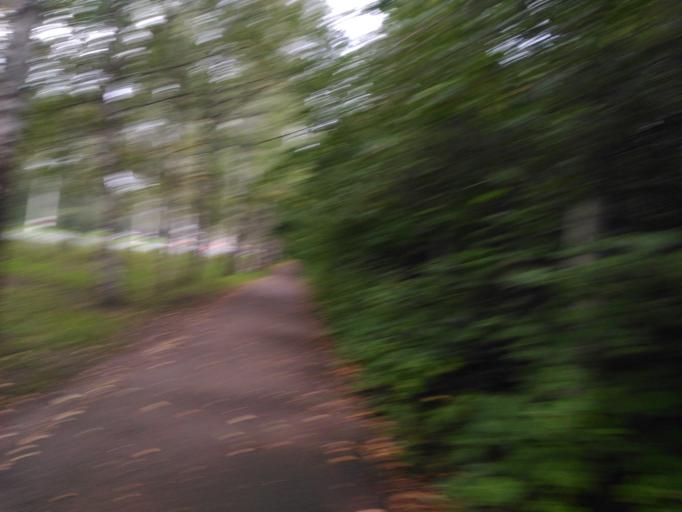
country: RU
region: Ulyanovsk
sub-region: Ulyanovskiy Rayon
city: Ulyanovsk
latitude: 54.2699
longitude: 48.3350
